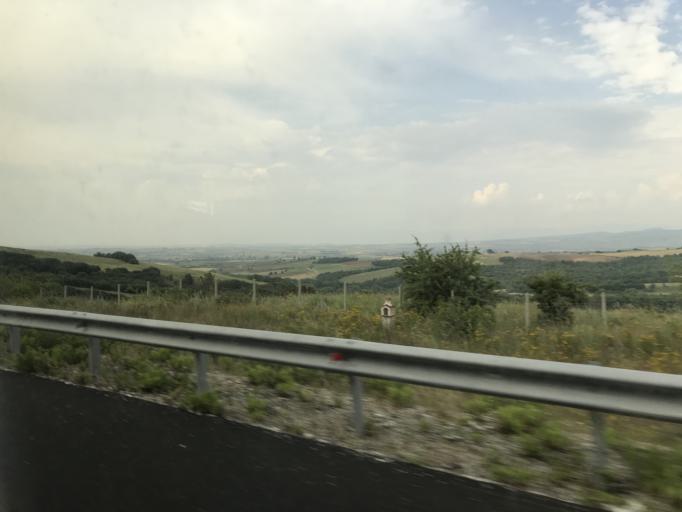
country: GR
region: East Macedonia and Thrace
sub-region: Nomos Rodopis
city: Sapes
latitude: 40.9479
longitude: 25.6609
